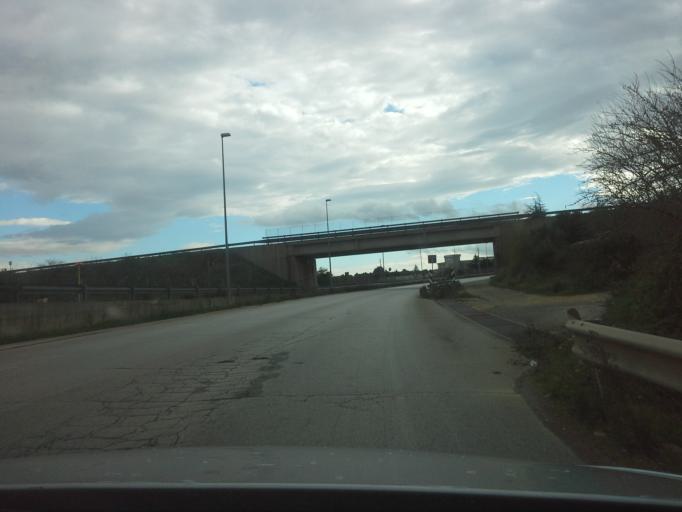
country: IT
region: Apulia
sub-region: Provincia di Bari
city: Turi
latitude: 40.9252
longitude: 16.9982
